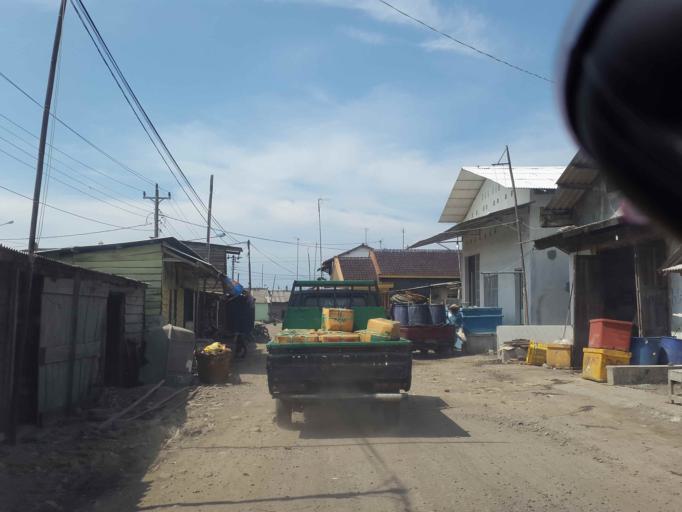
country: ID
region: Central Java
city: Tegal
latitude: -6.8523
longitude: 109.1277
